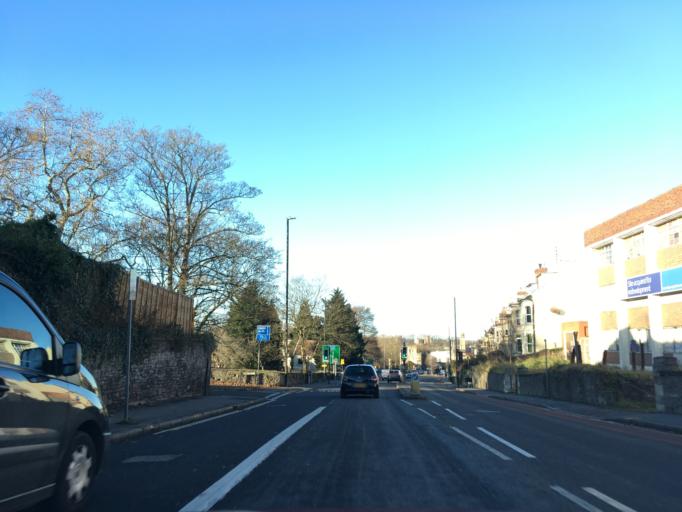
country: GB
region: England
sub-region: Bath and North East Somerset
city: Whitchurch
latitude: 51.4398
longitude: -2.5590
